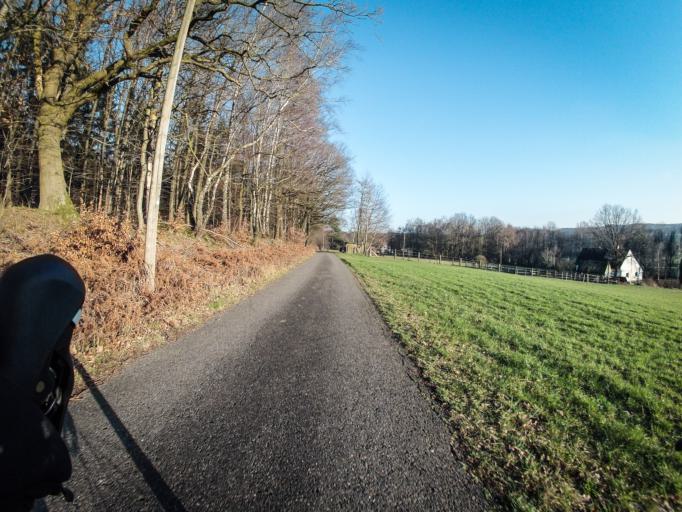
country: DE
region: North Rhine-Westphalia
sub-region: Regierungsbezirk Munster
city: Tecklenburg
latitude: 52.2413
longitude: 7.8541
